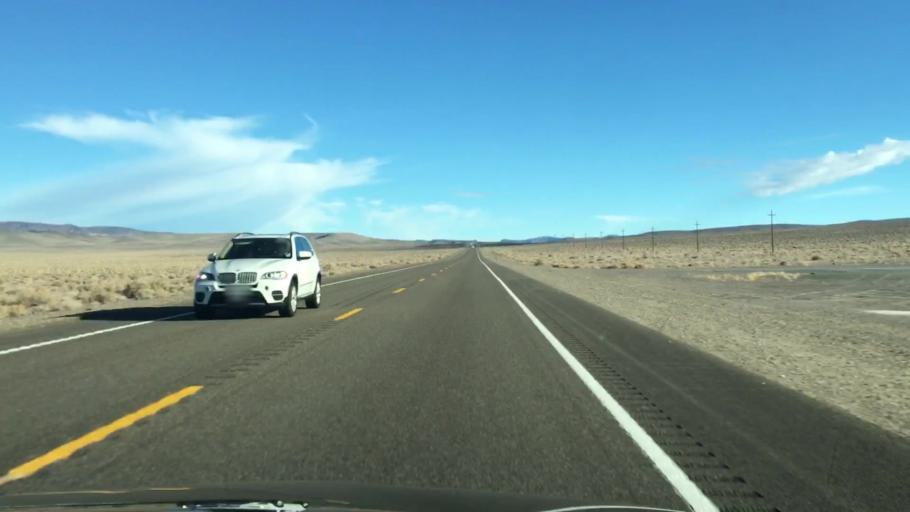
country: US
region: Nevada
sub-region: Mineral County
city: Hawthorne
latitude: 38.2535
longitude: -118.0797
